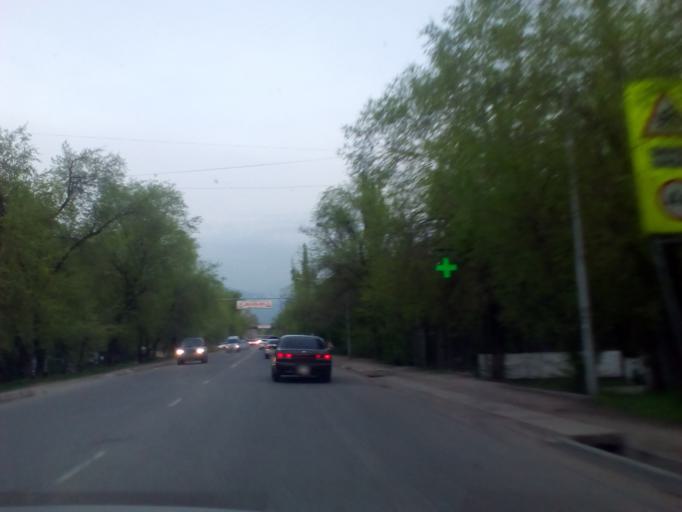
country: KZ
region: Almaty Qalasy
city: Almaty
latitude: 43.2359
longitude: 76.8245
